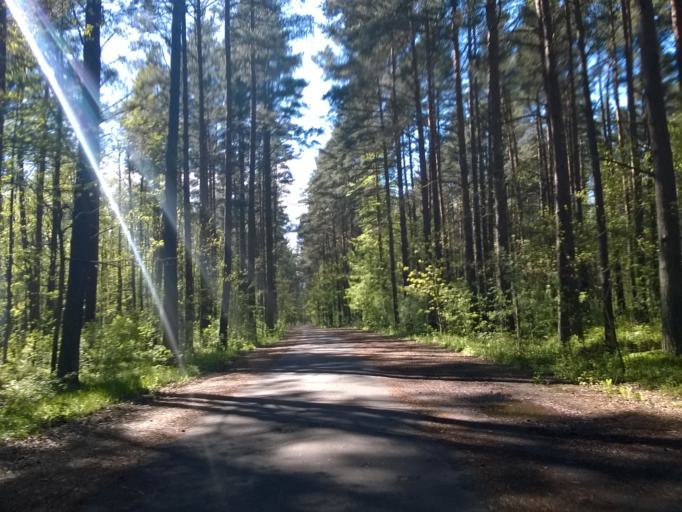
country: LV
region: Jurmala
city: Jurmala
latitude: 56.9594
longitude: 23.6435
